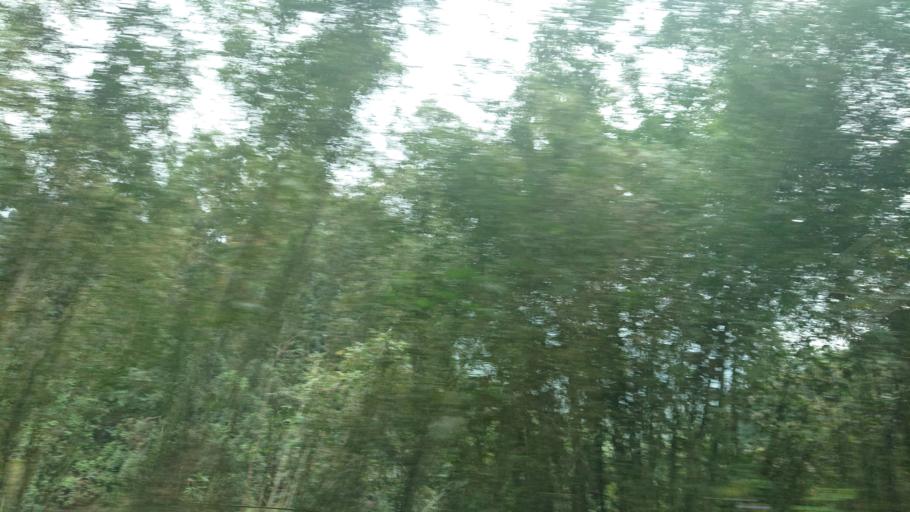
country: TW
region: Taiwan
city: Lugu
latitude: 23.6128
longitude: 120.7130
